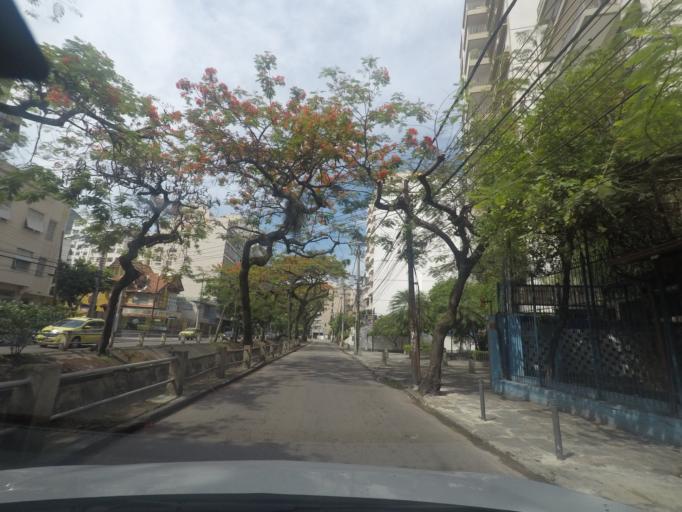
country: BR
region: Rio de Janeiro
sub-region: Rio De Janeiro
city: Rio de Janeiro
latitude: -22.9298
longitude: -43.2413
